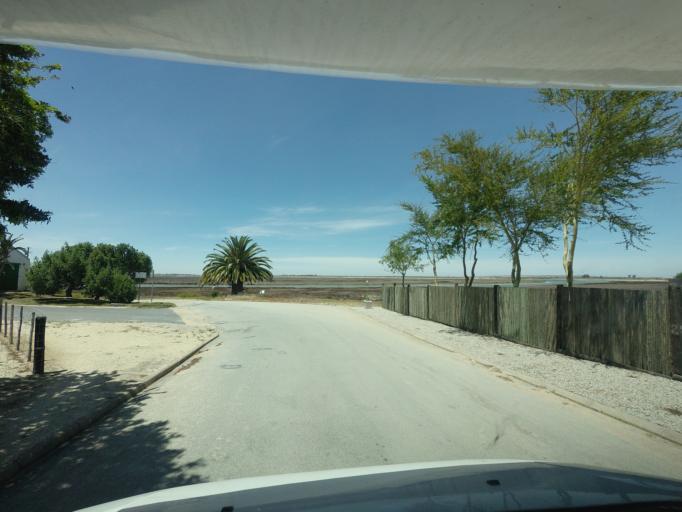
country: ZA
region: Western Cape
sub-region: West Coast District Municipality
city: Vredenburg
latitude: -32.7879
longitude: 18.1831
